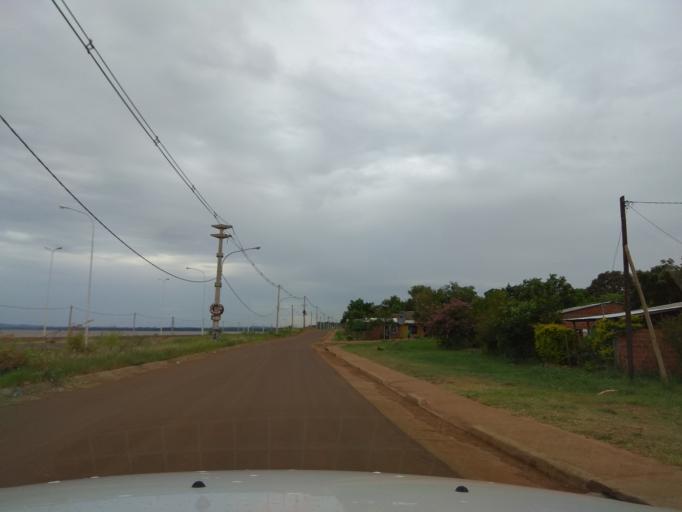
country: AR
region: Misiones
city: Garupa
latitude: -27.4369
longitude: -55.8586
